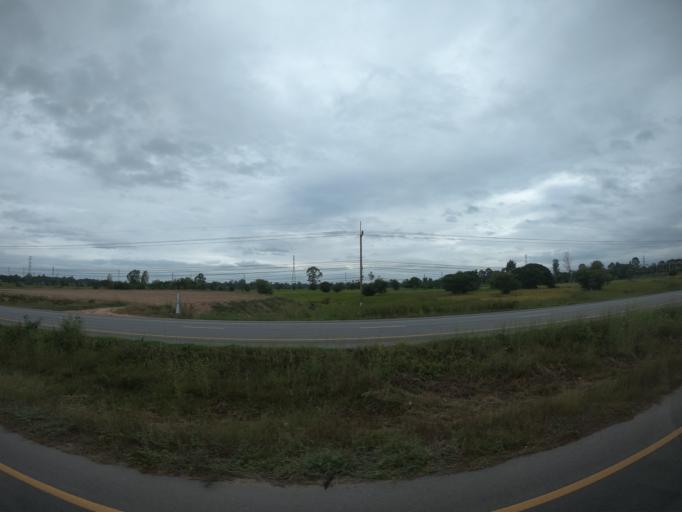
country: TH
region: Roi Et
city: Changhan
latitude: 16.1036
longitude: 103.5207
